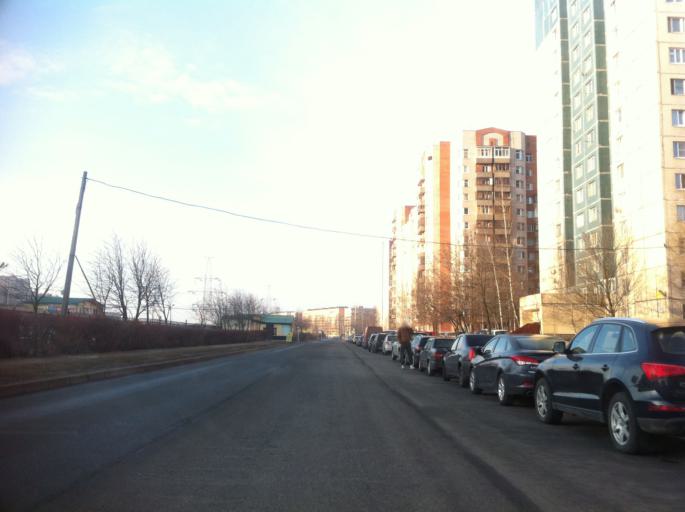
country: RU
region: St.-Petersburg
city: Uritsk
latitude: 59.8552
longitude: 30.1984
